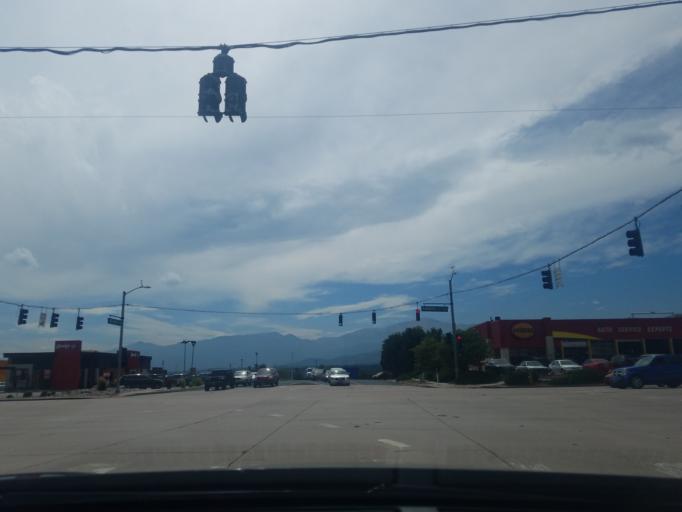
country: US
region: Colorado
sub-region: El Paso County
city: Air Force Academy
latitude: 38.9488
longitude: -104.8034
